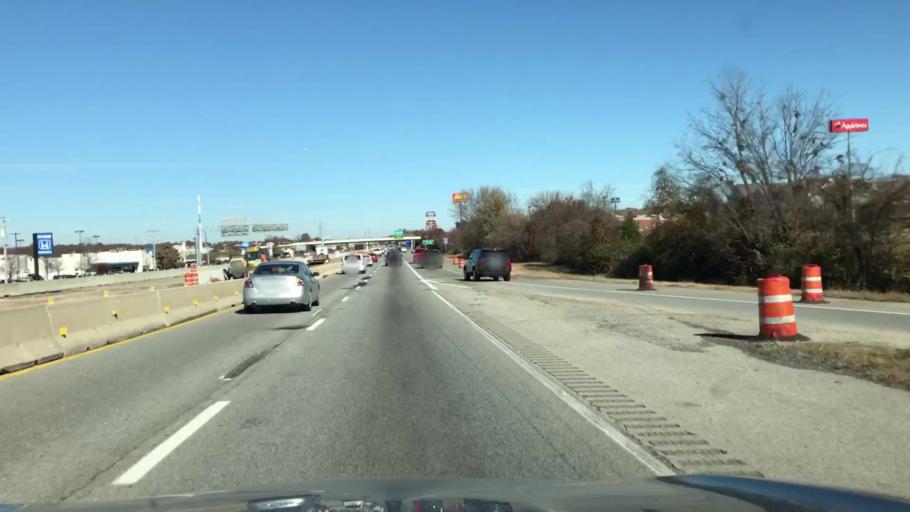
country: US
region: Arkansas
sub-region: Benton County
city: Bentonville
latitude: 36.3378
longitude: -94.1825
